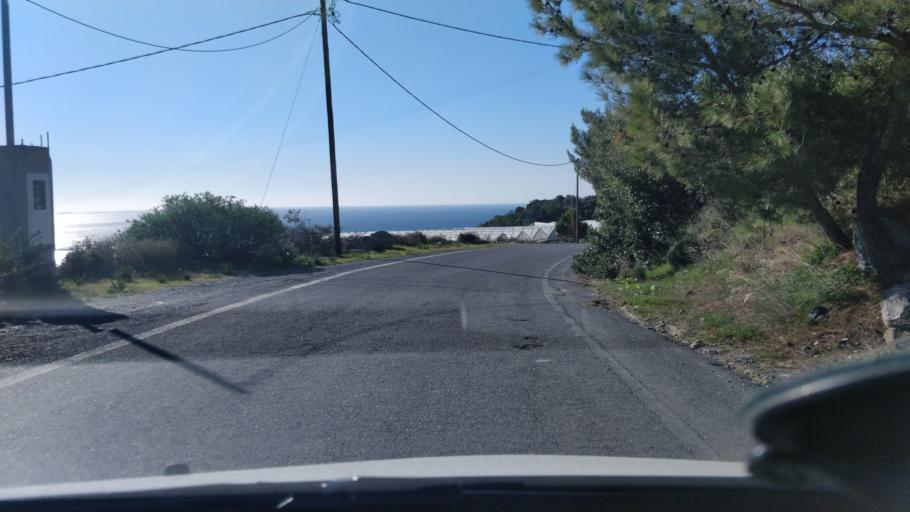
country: GR
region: Crete
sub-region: Nomos Lasithiou
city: Gra Liyia
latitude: 35.0374
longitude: 25.6700
